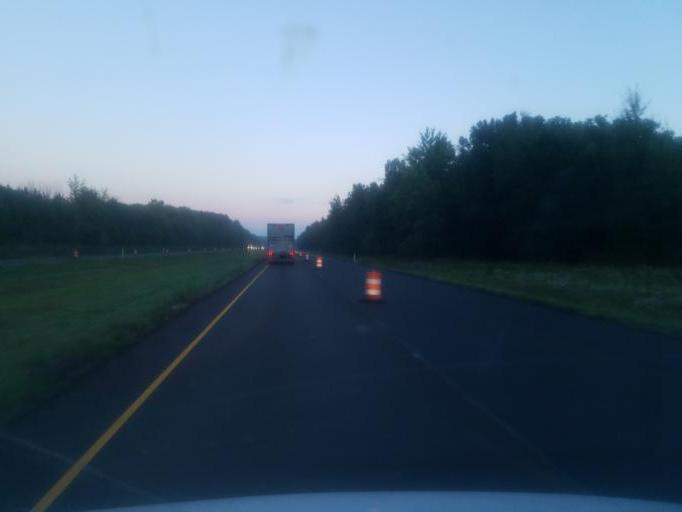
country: US
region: Ohio
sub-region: Ashtabula County
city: Jefferson
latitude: 41.7734
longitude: -80.7267
